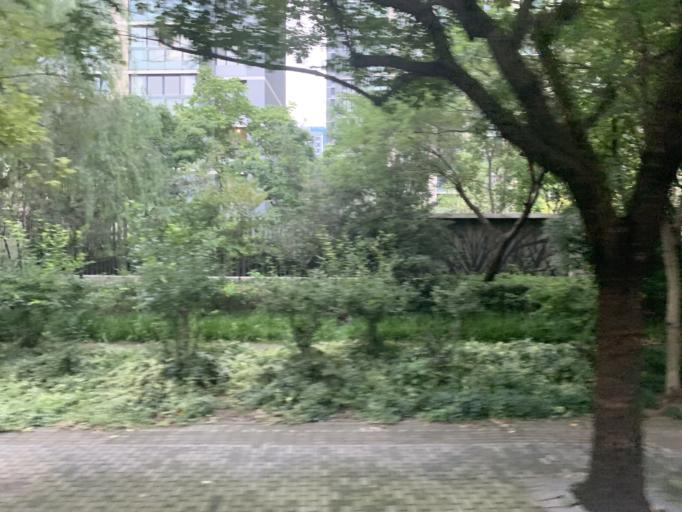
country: CN
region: Shanghai Shi
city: Pudong
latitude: 31.2410
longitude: 121.5357
